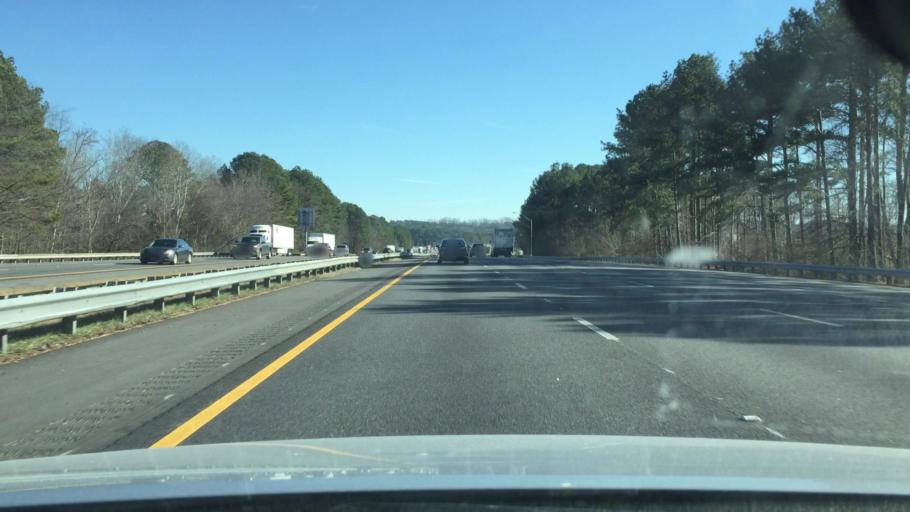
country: US
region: Georgia
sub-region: Catoosa County
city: Ringgold
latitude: 34.8850
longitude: -85.0598
